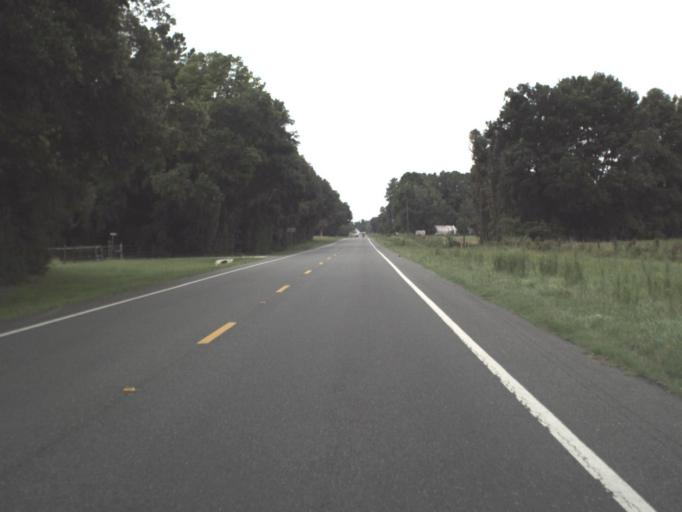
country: US
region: Florida
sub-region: Levy County
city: Williston
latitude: 29.3462
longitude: -82.4558
